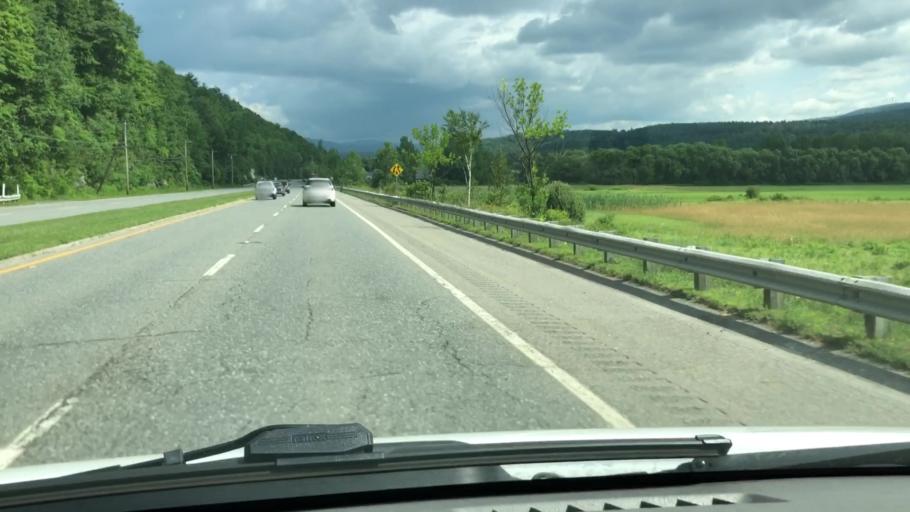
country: US
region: Massachusetts
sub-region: Berkshire County
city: North Adams
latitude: 42.6731
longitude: -73.1073
